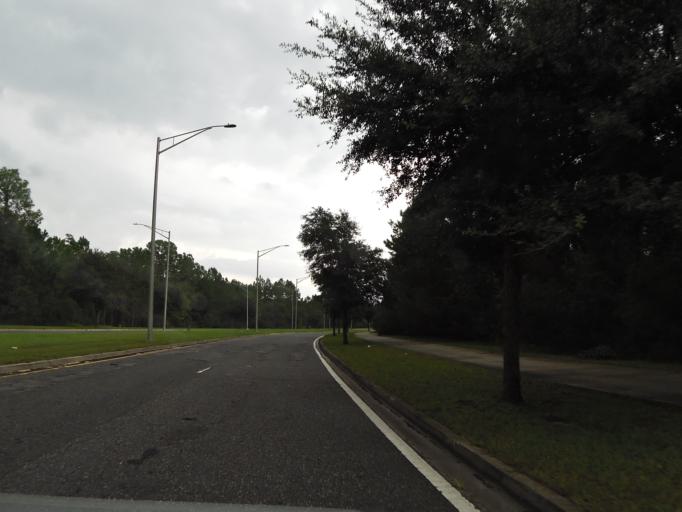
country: US
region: Florida
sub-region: Clay County
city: Lakeside
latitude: 30.1933
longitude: -81.8465
